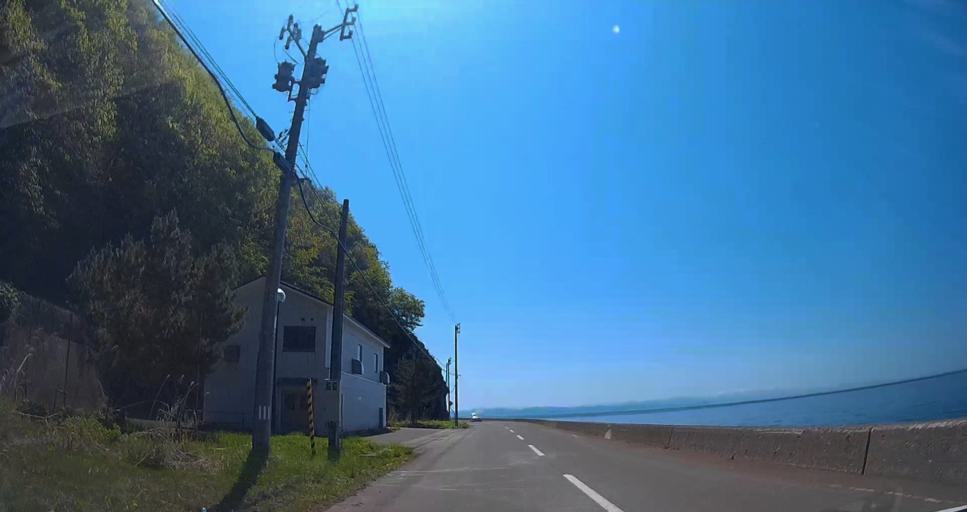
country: JP
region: Aomori
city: Aomori Shi
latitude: 41.1307
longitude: 140.7962
